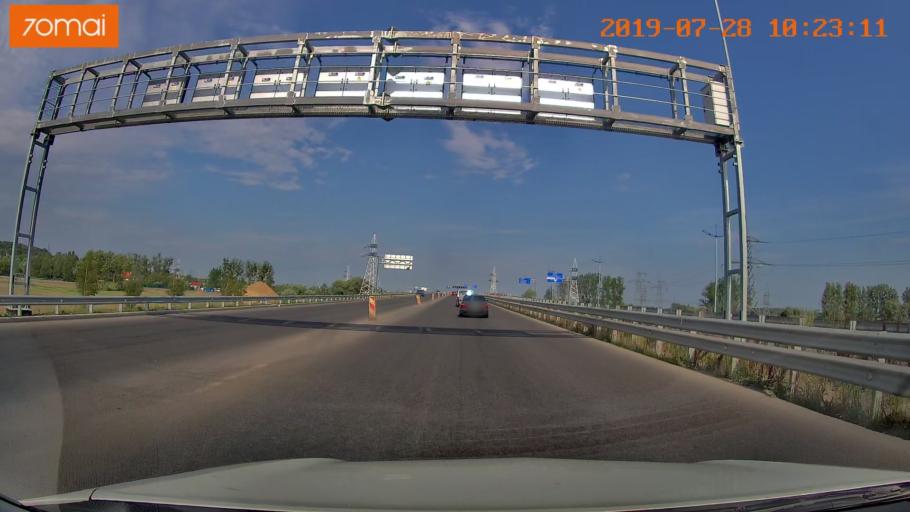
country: RU
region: Kaliningrad
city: Maloye Isakovo
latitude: 54.7655
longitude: 20.5627
